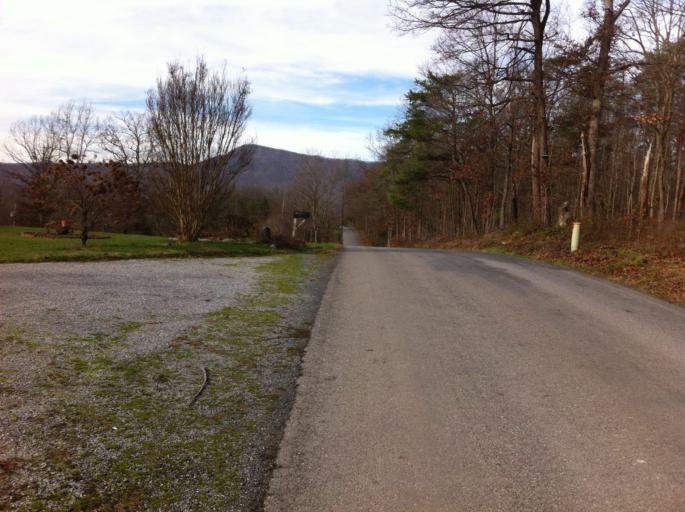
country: US
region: Virginia
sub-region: Page County
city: Luray
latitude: 38.7180
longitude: -78.4395
